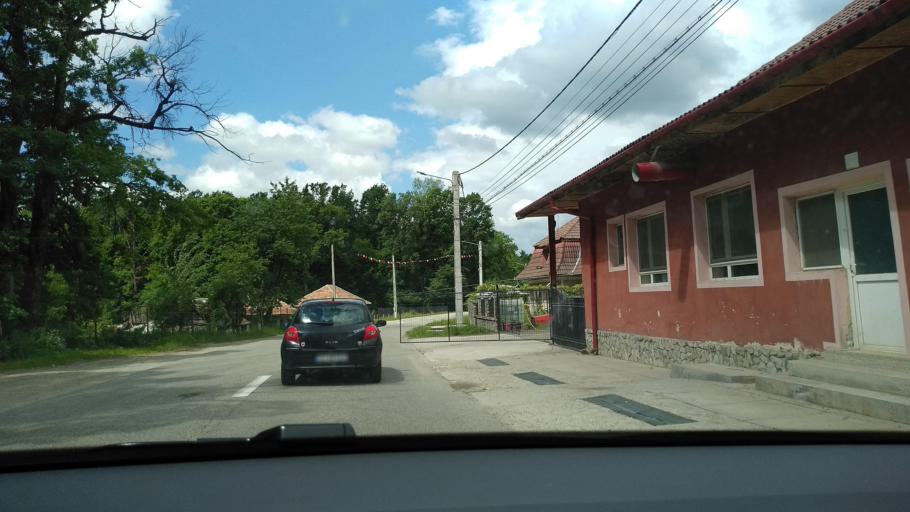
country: RO
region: Gorj
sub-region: Novaci
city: Pociovalistea
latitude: 45.1704
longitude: 23.6514
